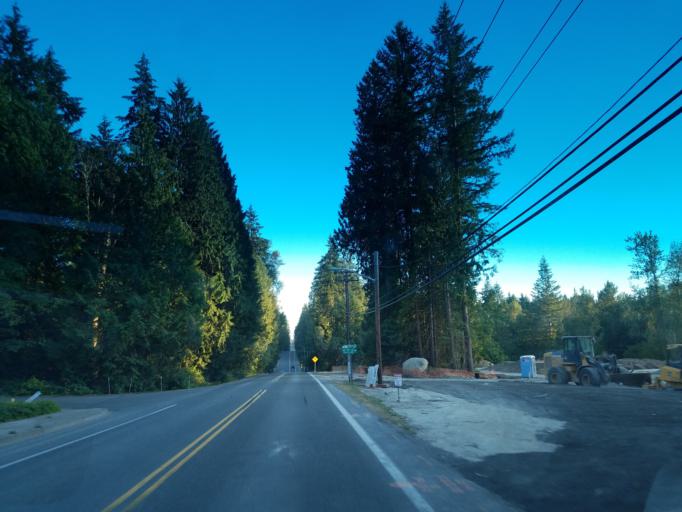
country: US
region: Washington
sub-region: King County
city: City of Sammamish
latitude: 47.6318
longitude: -122.0139
